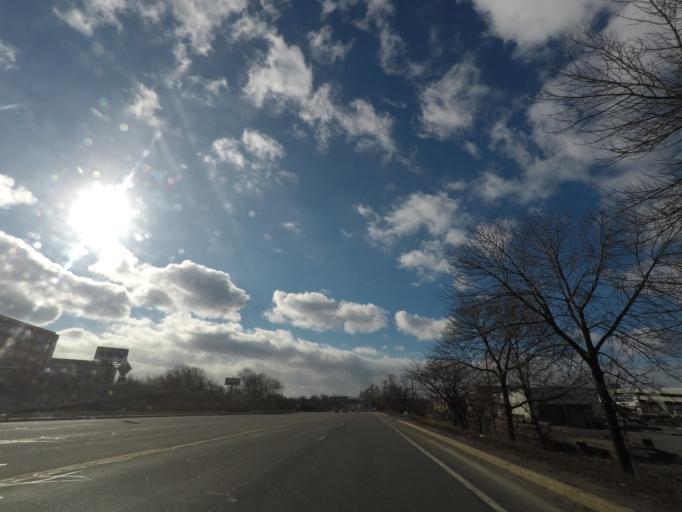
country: US
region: New York
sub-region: Schenectady County
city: Schenectady
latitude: 42.8234
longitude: -73.9327
